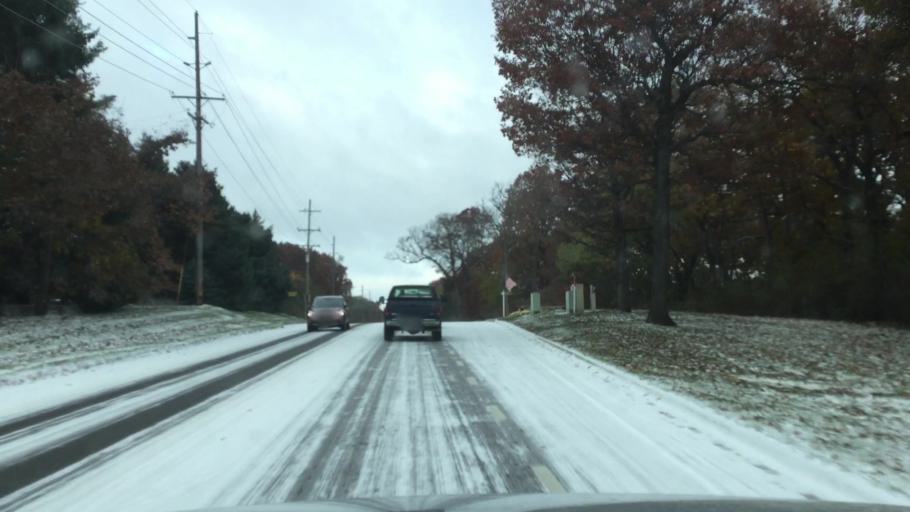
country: US
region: Michigan
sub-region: Livingston County
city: Brighton
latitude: 42.5277
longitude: -83.8489
